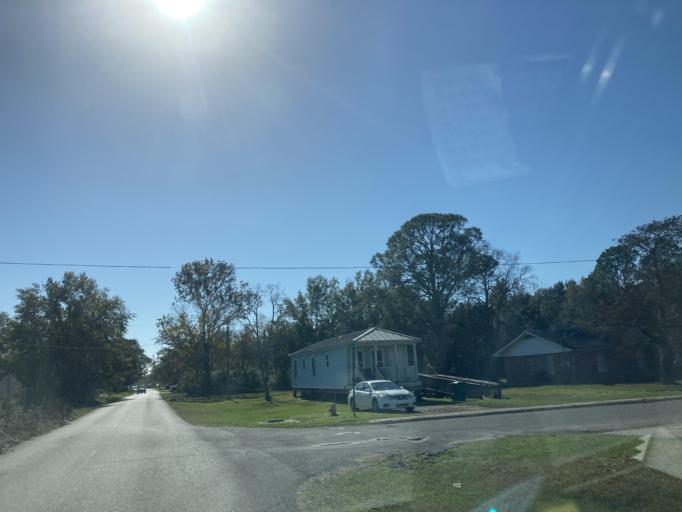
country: US
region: Mississippi
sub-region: Harrison County
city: West Gulfport
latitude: 30.3904
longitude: -89.0868
